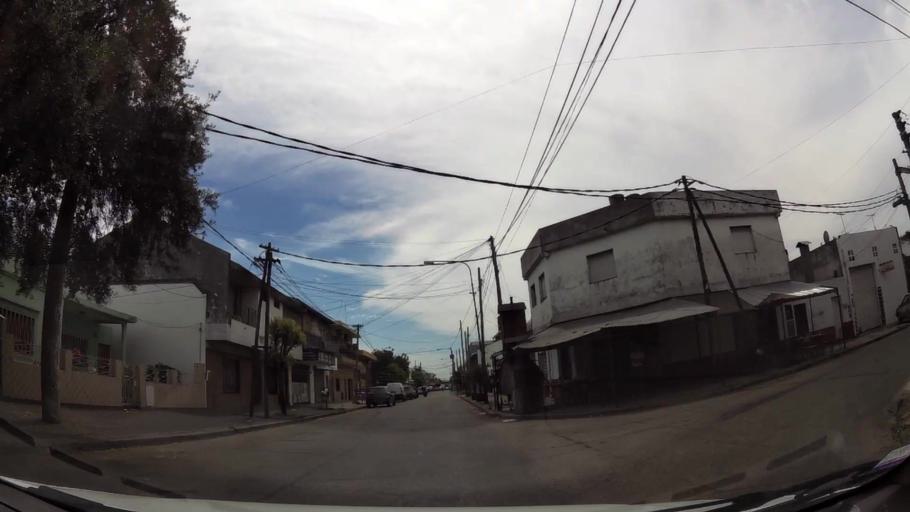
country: AR
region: Buenos Aires
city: San Justo
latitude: -34.6801
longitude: -58.5386
